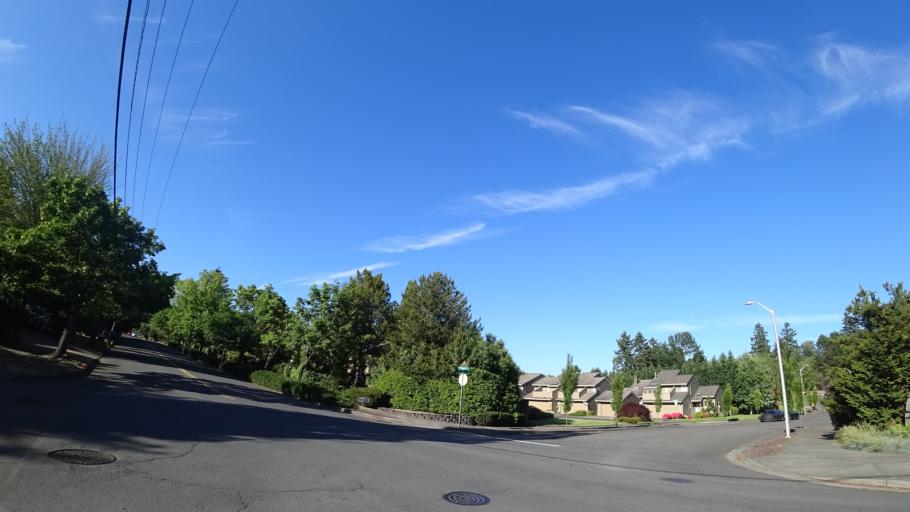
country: US
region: Oregon
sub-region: Washington County
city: Beaverton
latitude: 45.4627
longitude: -122.8081
